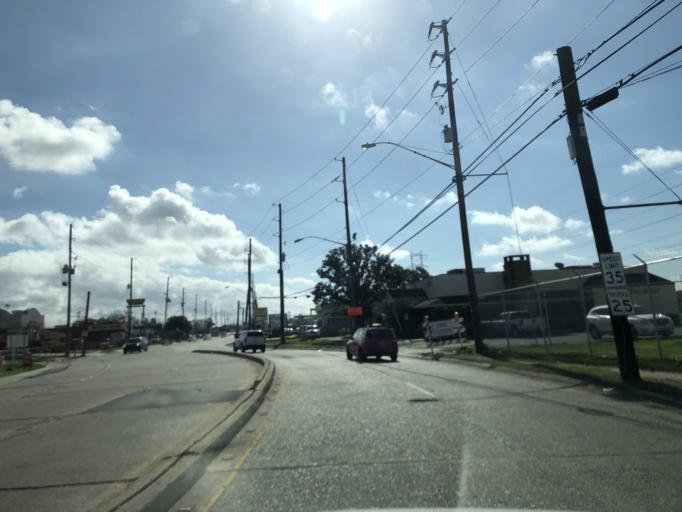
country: US
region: Louisiana
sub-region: Jefferson Parish
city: Kenner
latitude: 30.0049
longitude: -90.2208
